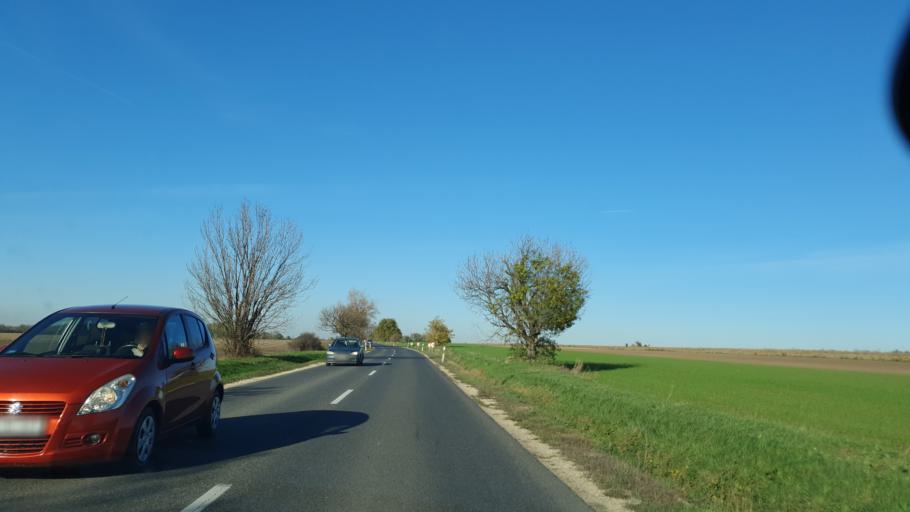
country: HU
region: Fejer
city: Szekesfehervar
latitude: 47.2529
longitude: 18.4192
